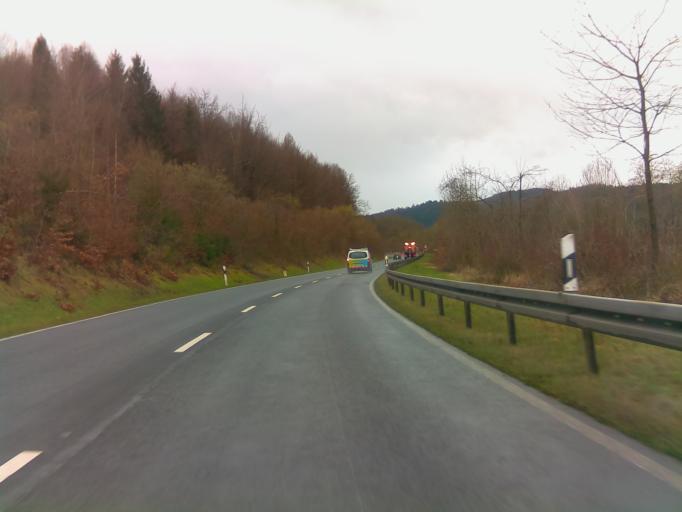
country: DE
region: Hesse
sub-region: Regierungsbezirk Darmstadt
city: Steinau an der Strasse
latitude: 50.3039
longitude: 9.4282
